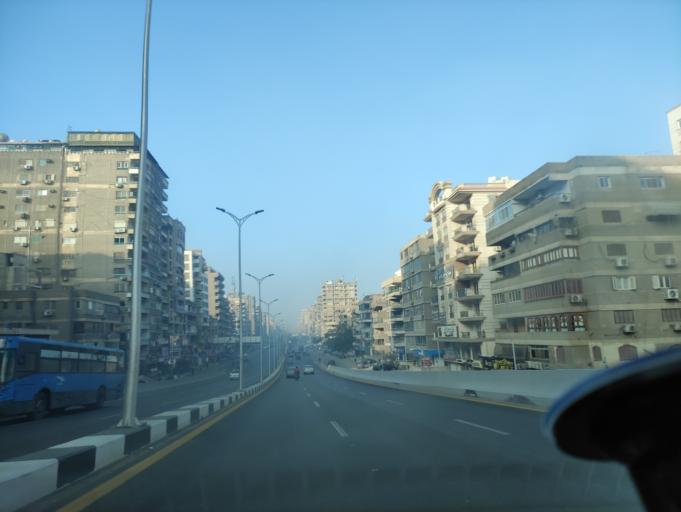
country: EG
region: Muhafazat al Qahirah
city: Cairo
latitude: 30.0546
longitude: 31.3454
